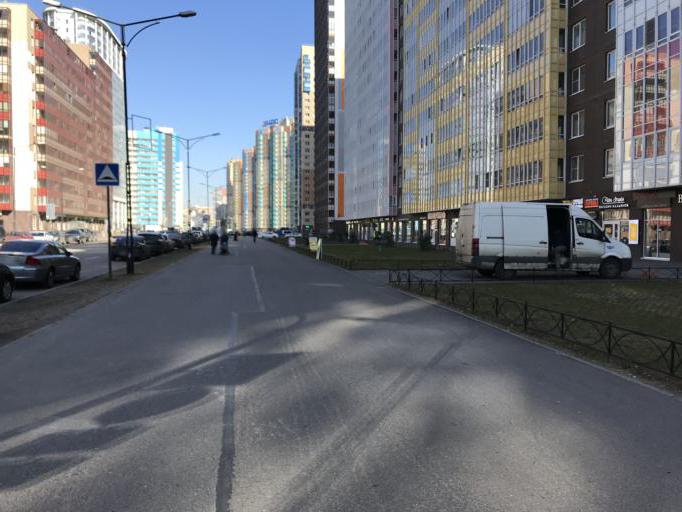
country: RU
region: Leningrad
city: Rybatskoye
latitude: 59.9008
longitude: 30.5117
